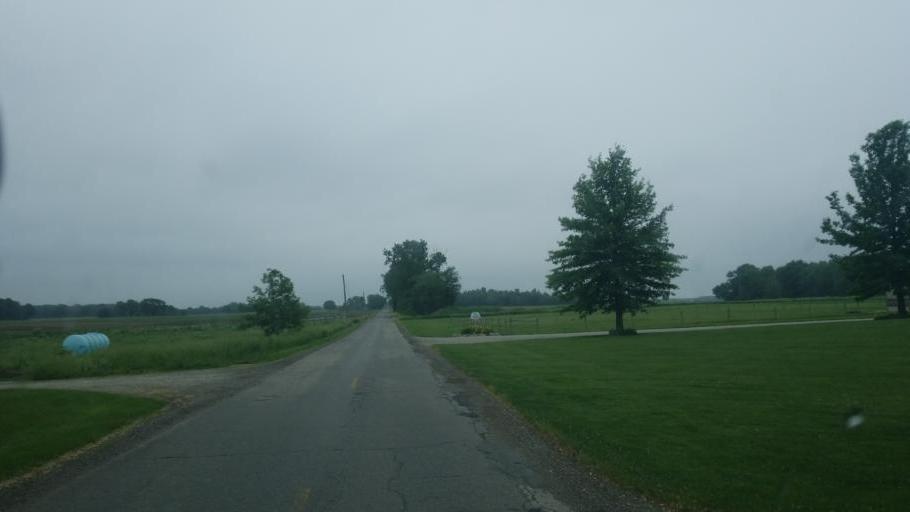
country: US
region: Indiana
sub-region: Marshall County
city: Bremen
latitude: 41.5029
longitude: -86.1179
